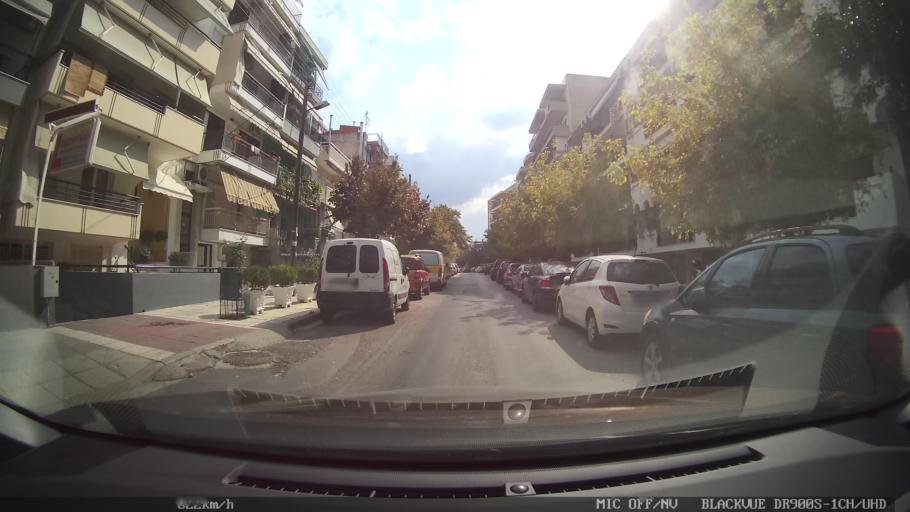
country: GR
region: Central Macedonia
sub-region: Nomos Thessalonikis
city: Triandria
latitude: 40.6127
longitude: 22.9855
